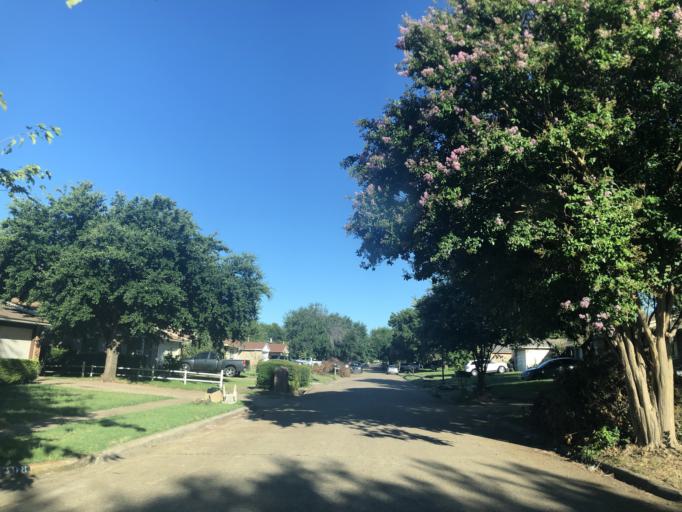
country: US
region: Texas
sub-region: Dallas County
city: Duncanville
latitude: 32.6438
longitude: -96.9487
